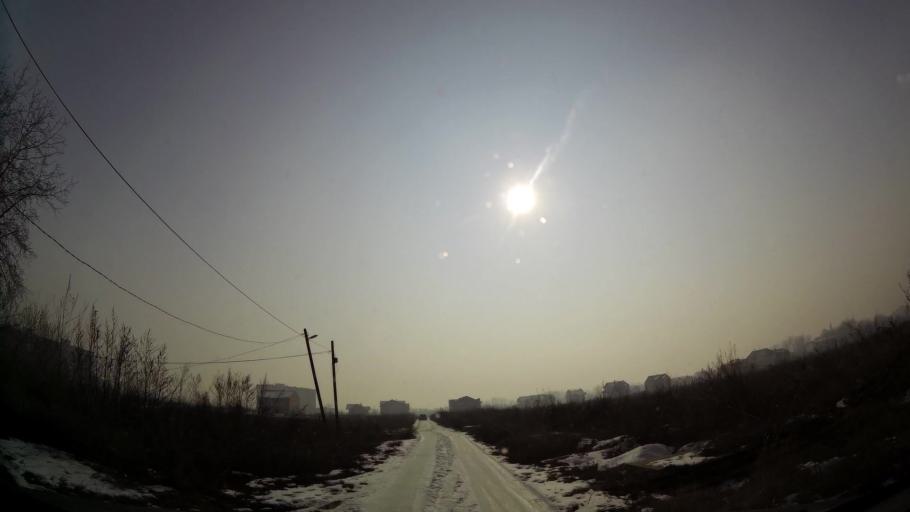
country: MK
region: Kisela Voda
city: Kisela Voda
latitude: 41.9950
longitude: 21.5171
